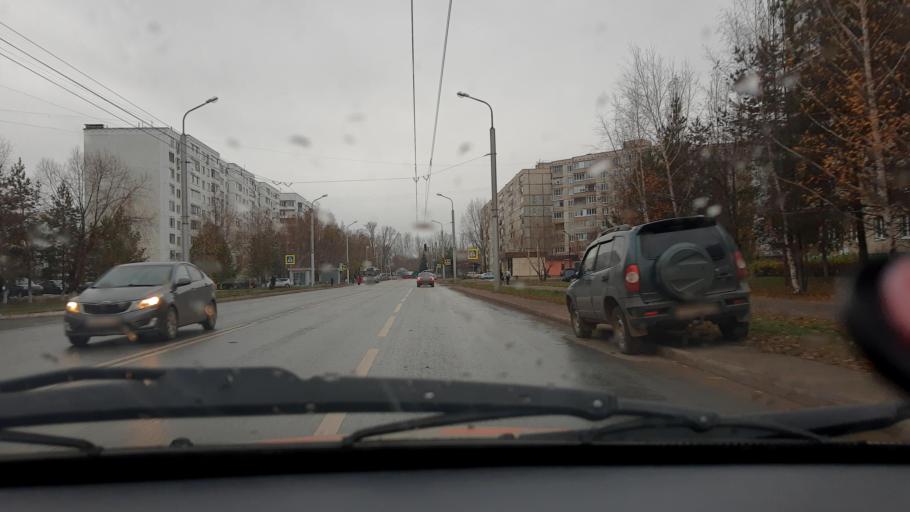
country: RU
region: Bashkortostan
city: Ufa
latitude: 54.7770
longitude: 56.1146
